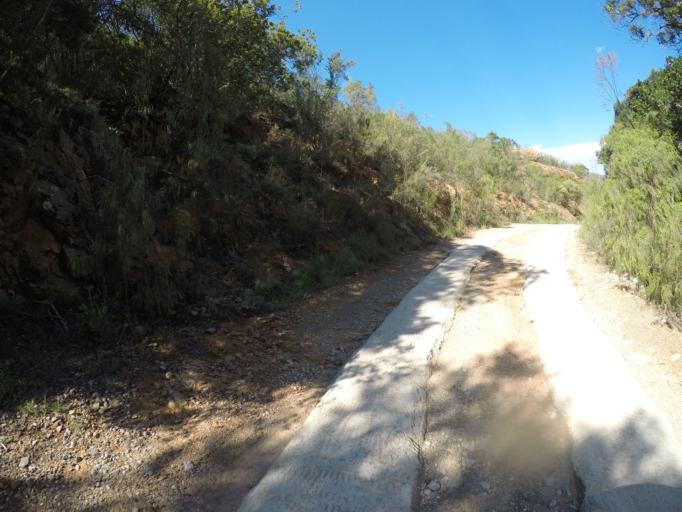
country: ZA
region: Eastern Cape
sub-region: Cacadu District Municipality
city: Kareedouw
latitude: -33.6429
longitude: 24.4623
